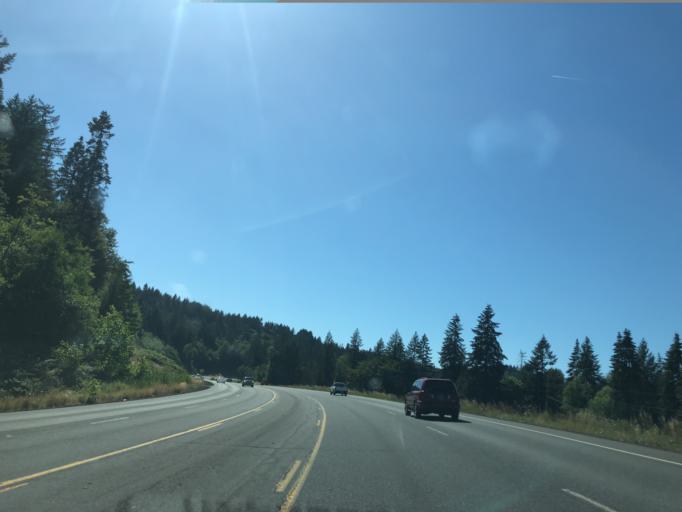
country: US
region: Oregon
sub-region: Linn County
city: Sweet Home
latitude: 44.4048
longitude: -122.7519
